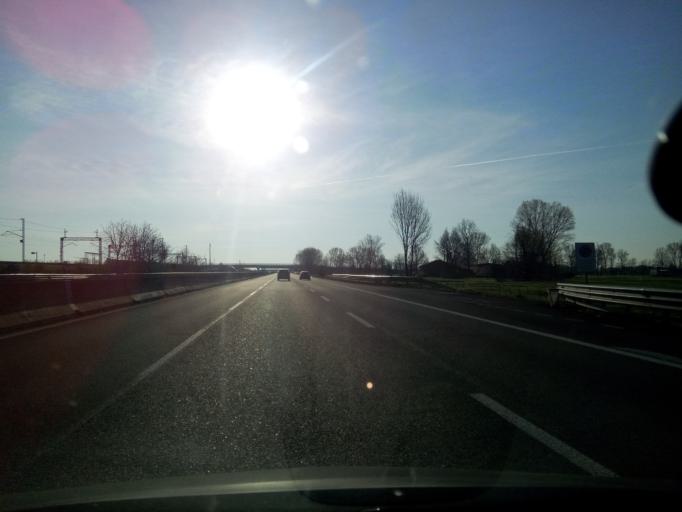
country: IT
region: Emilia-Romagna
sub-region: Provincia di Parma
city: Fontanellato
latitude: 44.8793
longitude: 10.1536
